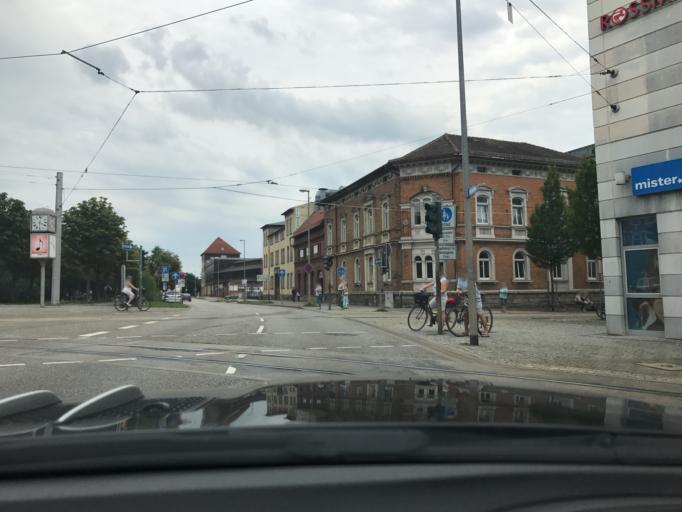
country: DE
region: Thuringia
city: Nordhausen
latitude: 51.4957
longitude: 10.7907
